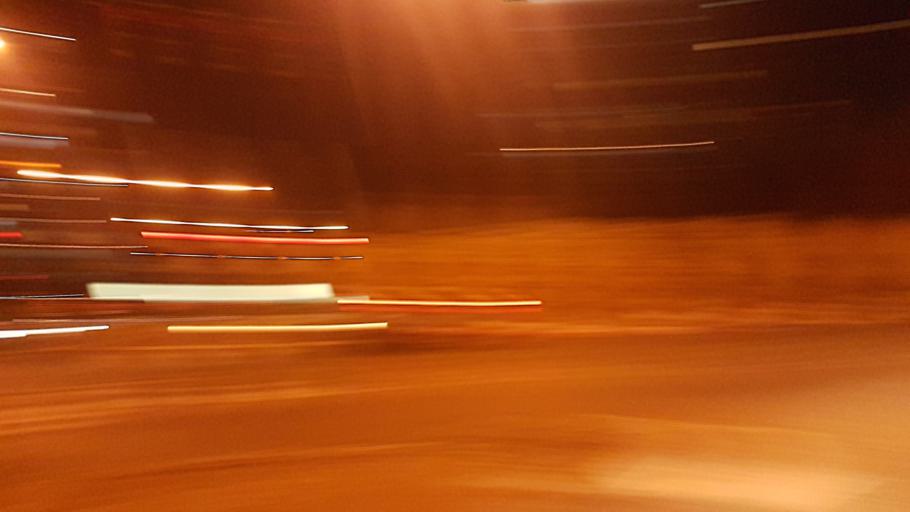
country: IL
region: Central District
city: Hod HaSharon
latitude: 32.1629
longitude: 34.8939
